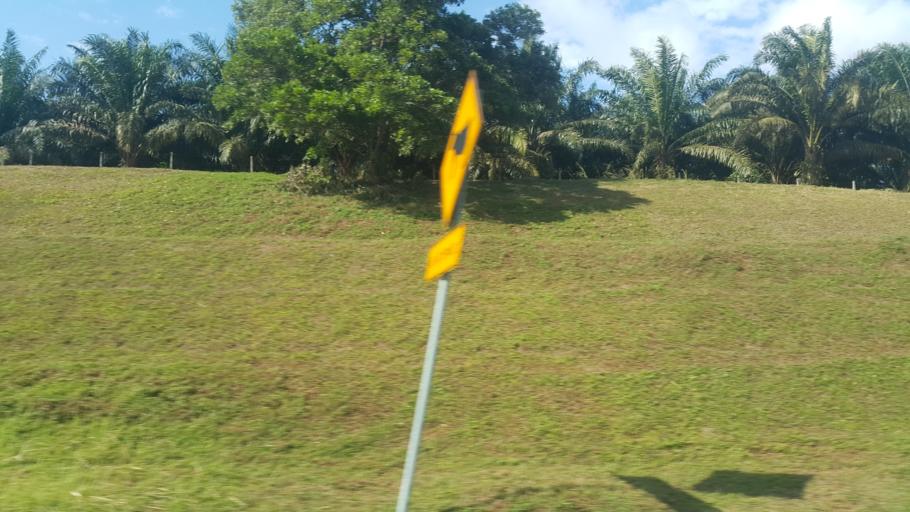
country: MY
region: Johor
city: Kelapa Sawit
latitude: 1.7320
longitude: 103.4190
